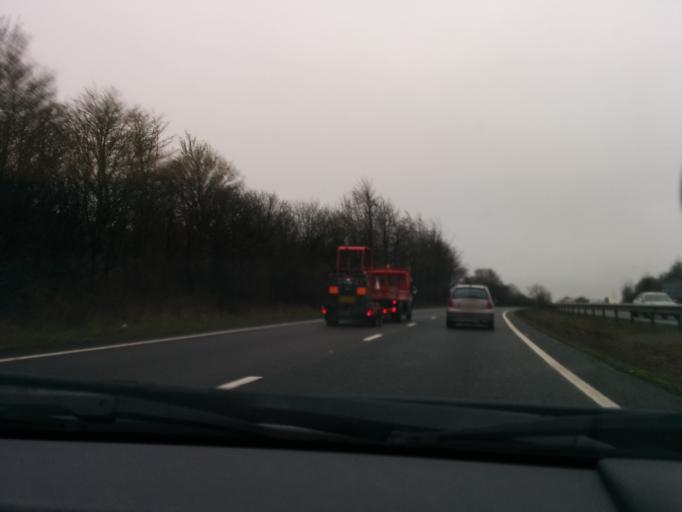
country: GB
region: England
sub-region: Hampshire
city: Highclere
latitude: 51.3128
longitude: -1.3335
